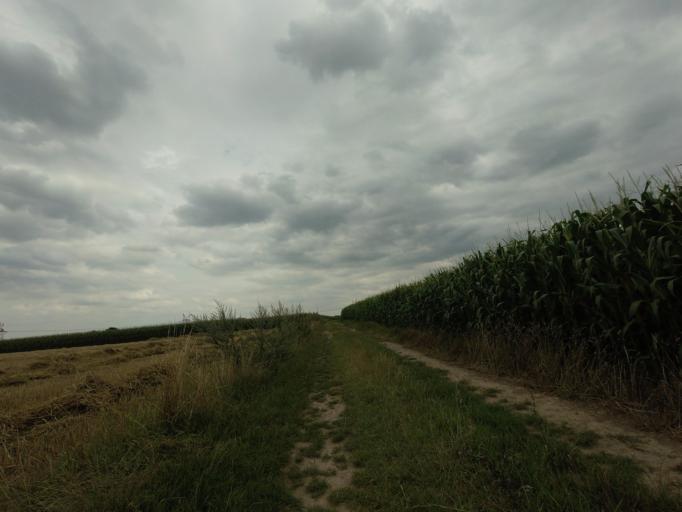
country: BE
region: Flanders
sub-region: Provincie Vlaams-Brabant
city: Grimbergen
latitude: 50.9248
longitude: 4.3832
